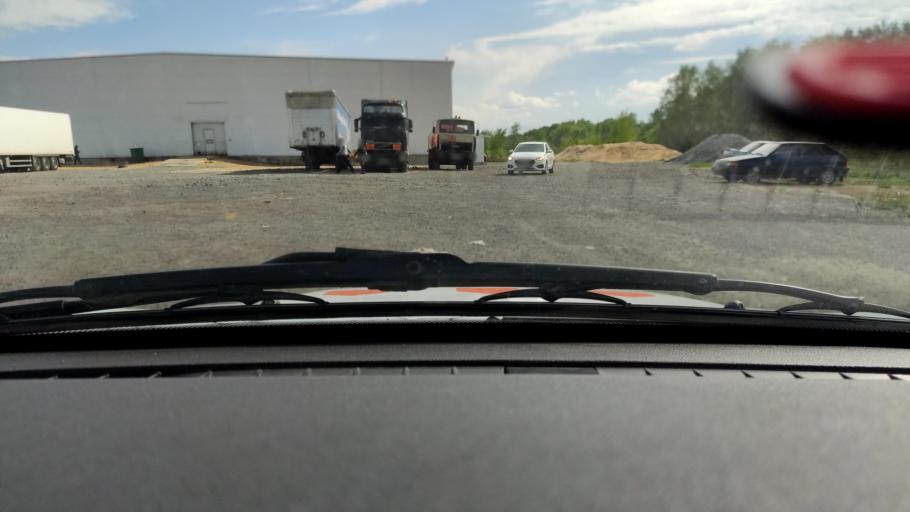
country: RU
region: Voronezj
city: Voronezh
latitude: 51.6736
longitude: 39.2749
